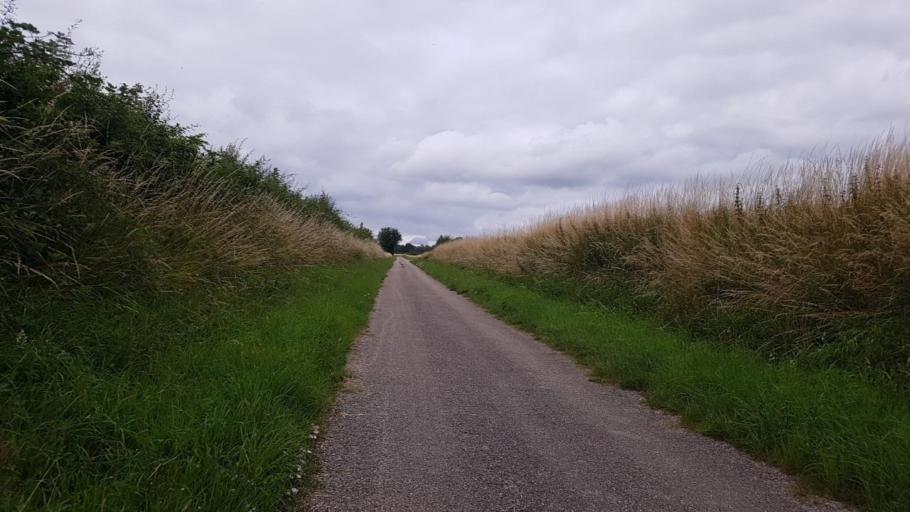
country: FR
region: Picardie
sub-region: Departement de l'Aisne
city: Origny-en-Thierache
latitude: 49.9293
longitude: 3.9947
